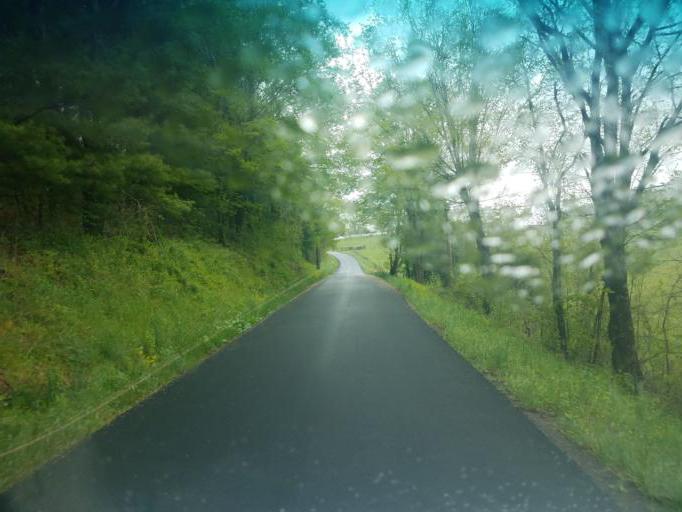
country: US
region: Virginia
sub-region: Smyth County
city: Marion
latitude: 36.9285
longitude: -81.5416
